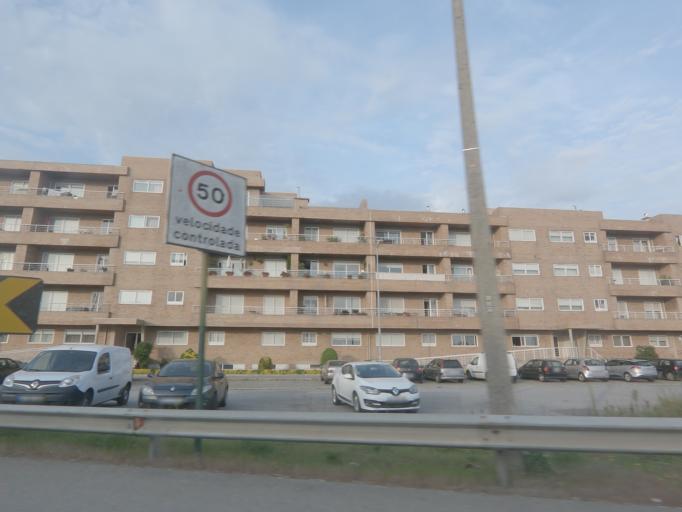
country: PT
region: Porto
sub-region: Gondomar
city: Baguim do Monte
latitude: 41.2043
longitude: -8.5275
